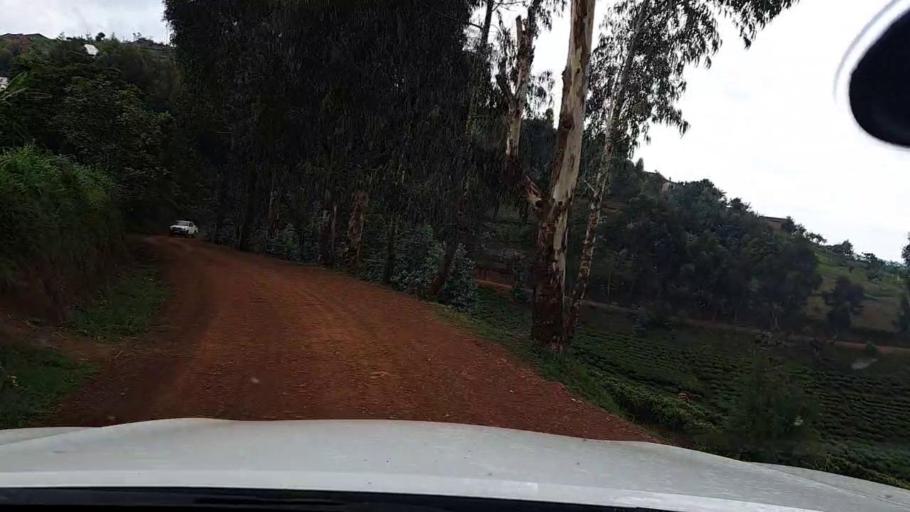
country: RW
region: Western Province
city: Kibuye
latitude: -2.1738
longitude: 29.4402
